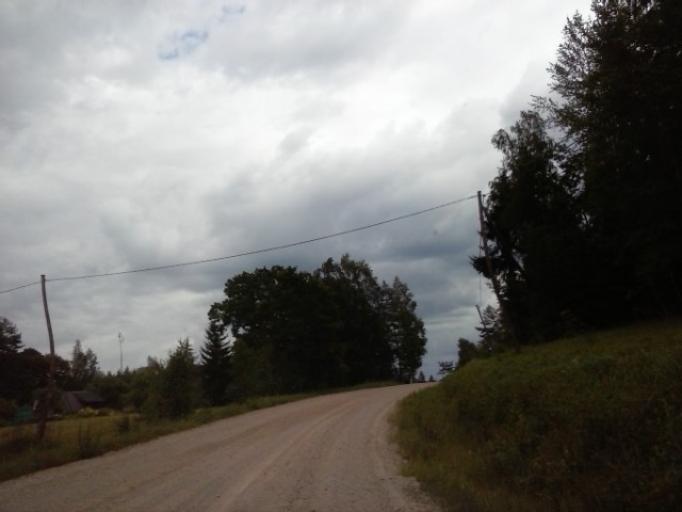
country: EE
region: Vorumaa
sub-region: Voru linn
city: Voru
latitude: 57.7445
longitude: 27.0859
